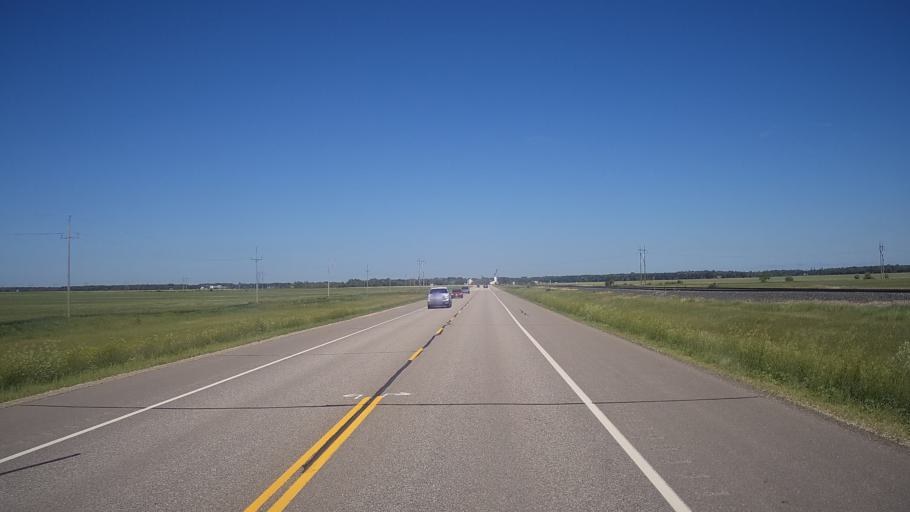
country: CA
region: Manitoba
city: Portage la Prairie
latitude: 50.1194
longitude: -98.5614
